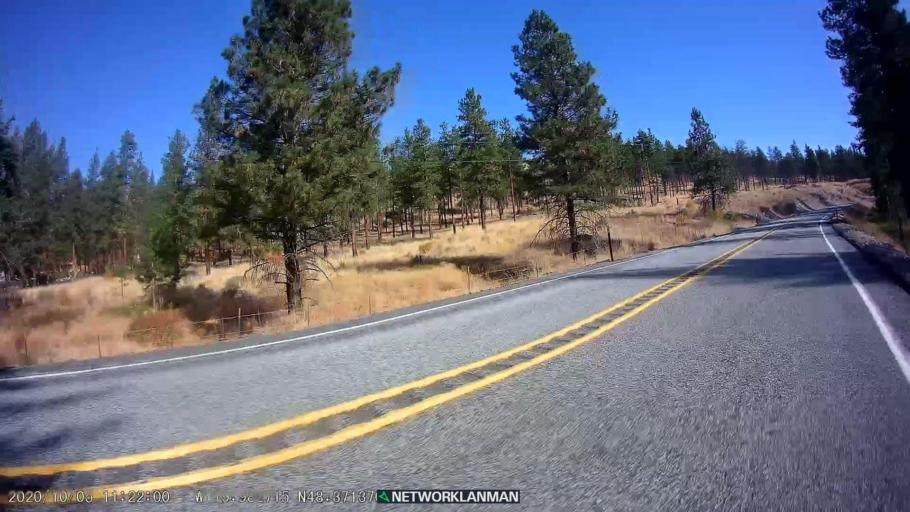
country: US
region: Washington
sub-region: Okanogan County
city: Brewster
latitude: 48.3716
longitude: -119.9819
